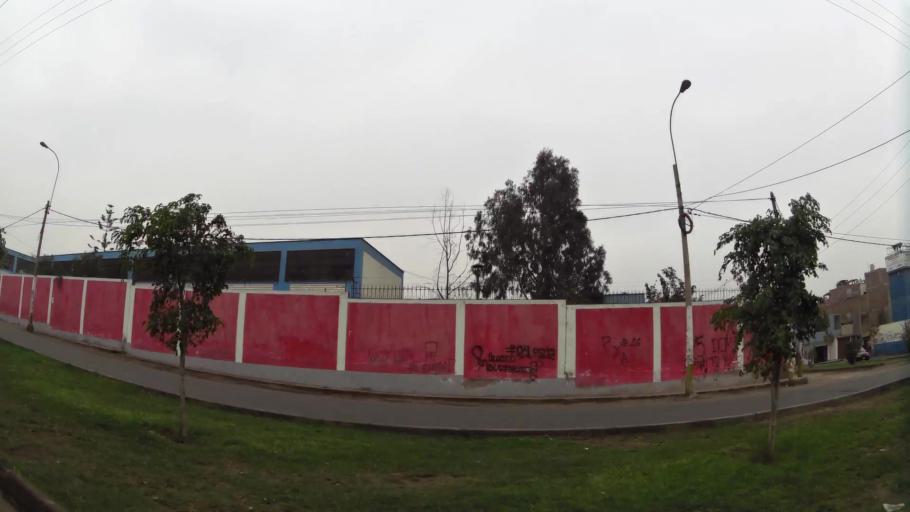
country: PE
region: Lima
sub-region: Lima
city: Independencia
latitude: -11.9581
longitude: -76.9903
